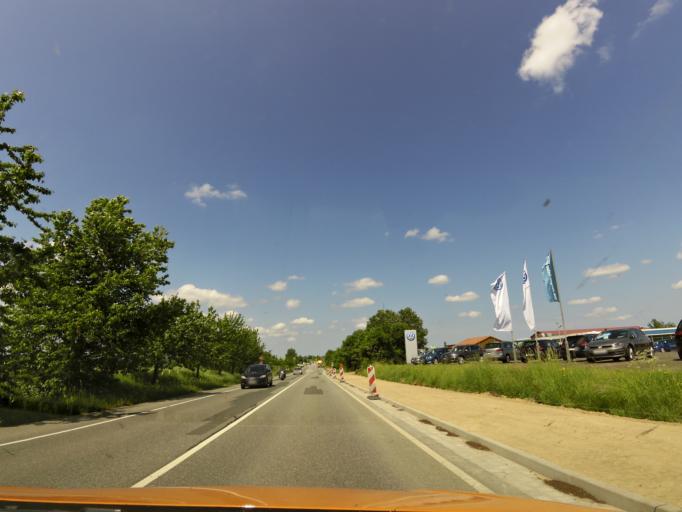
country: DE
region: Mecklenburg-Vorpommern
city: Gadebusch
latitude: 53.6825
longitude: 11.1378
